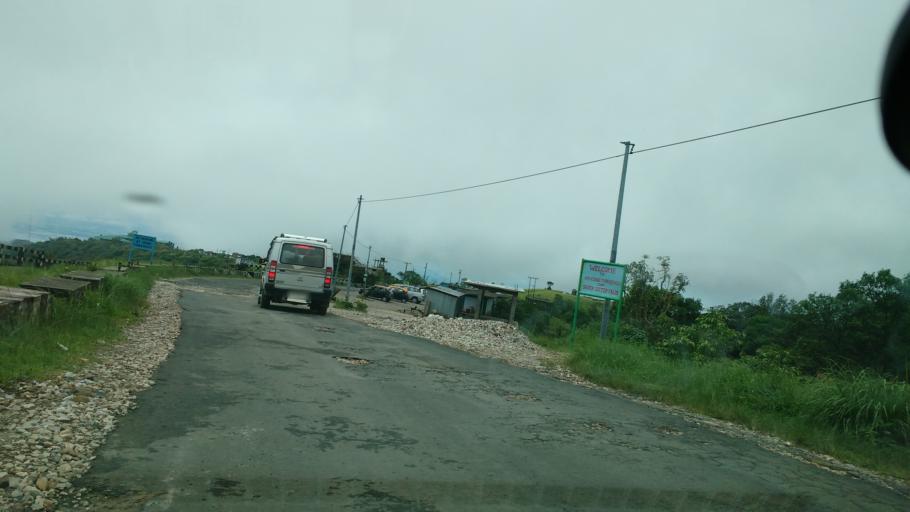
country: IN
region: Meghalaya
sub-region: East Khasi Hills
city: Cherrapunji
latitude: 25.2391
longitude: 91.7326
